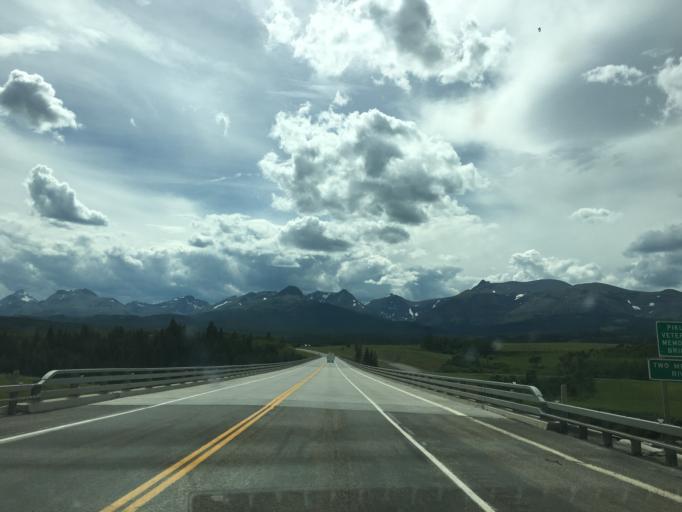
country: US
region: Montana
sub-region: Glacier County
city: South Browning
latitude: 48.4506
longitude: -113.2018
